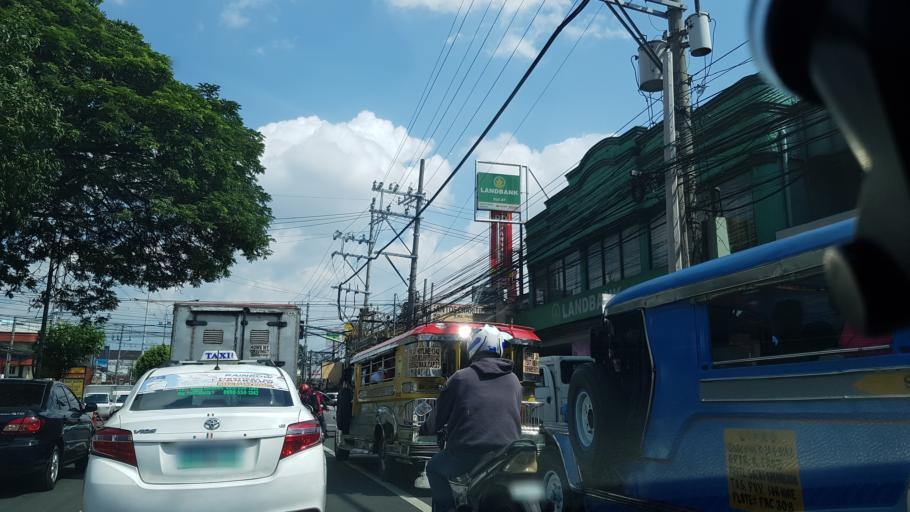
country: PH
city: Sambayanihan People's Village
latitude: 14.4713
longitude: 121.0074
